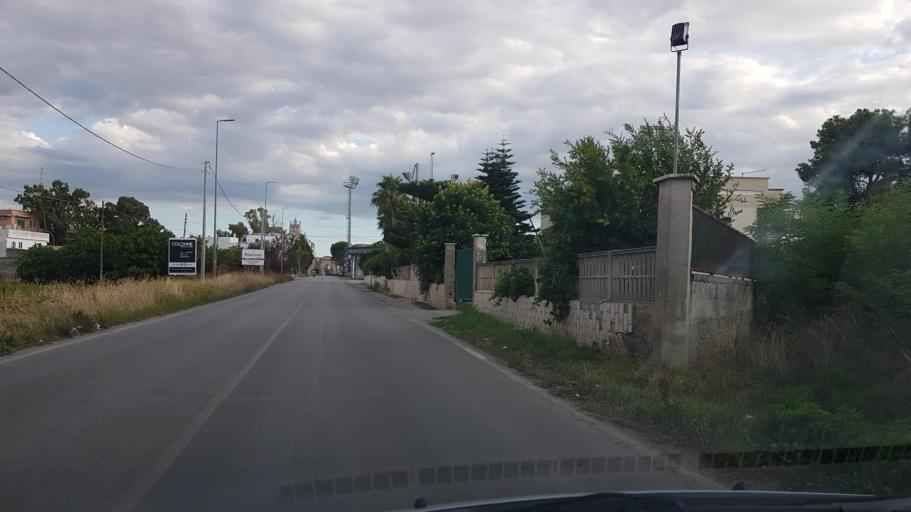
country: IT
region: Apulia
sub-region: Provincia di Brindisi
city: Francavilla Fontana
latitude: 40.5371
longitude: 17.5771
